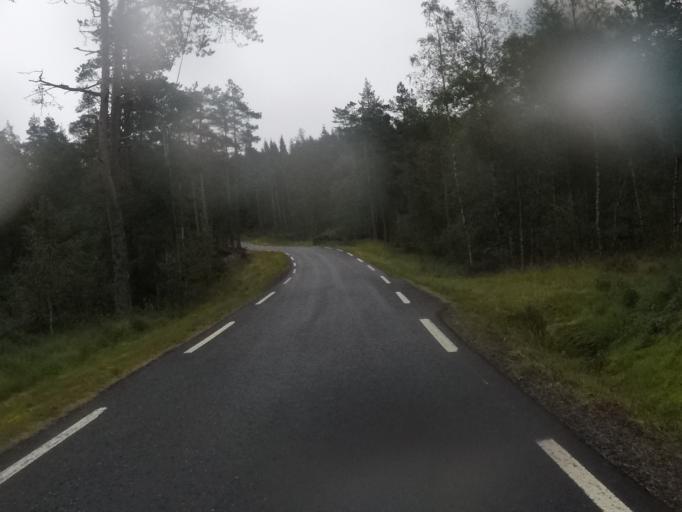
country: NO
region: Vest-Agder
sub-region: Kvinesdal
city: Liknes
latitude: 58.2578
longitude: 7.0296
